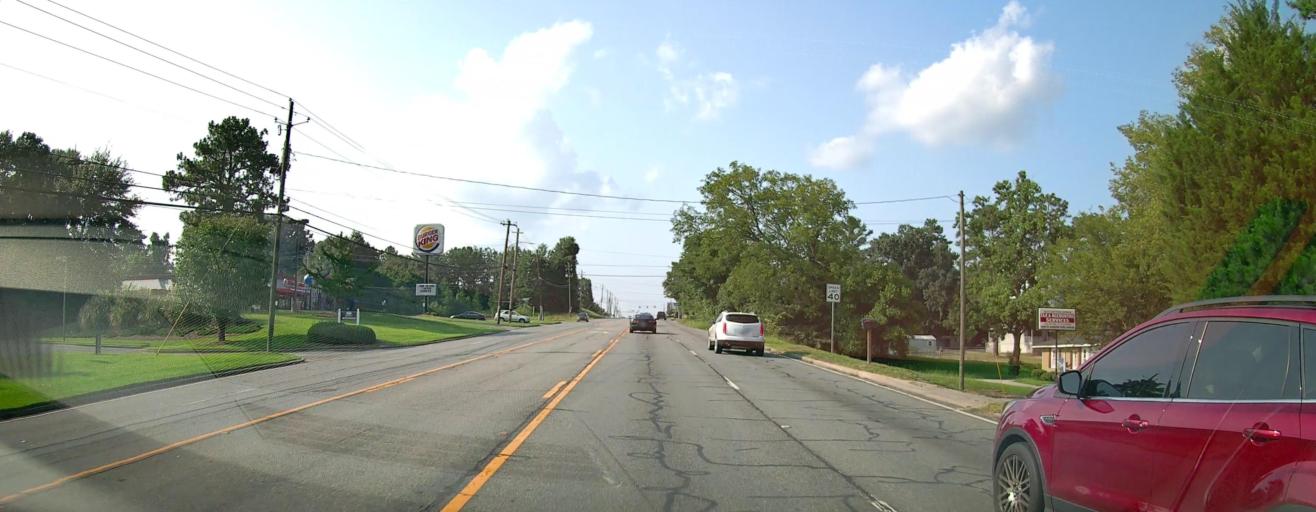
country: US
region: Georgia
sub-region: Bibb County
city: Macon
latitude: 32.8075
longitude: -83.6630
